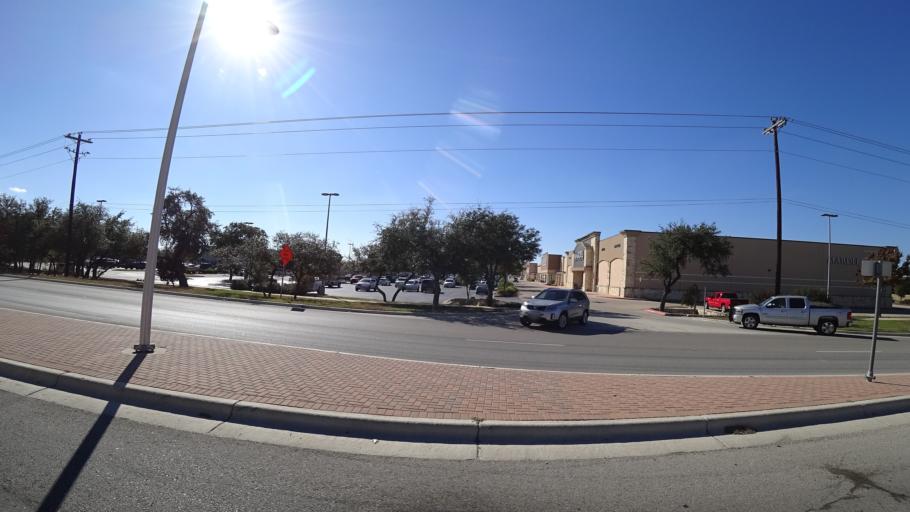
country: US
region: Texas
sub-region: Williamson County
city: Cedar Park
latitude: 30.5293
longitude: -97.8062
